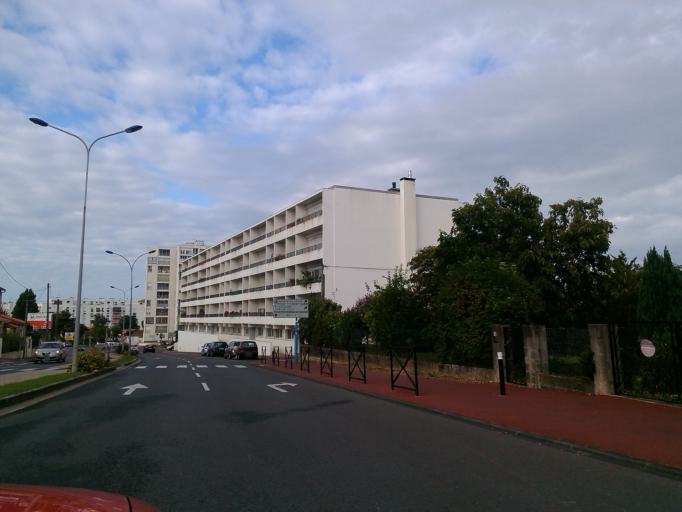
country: FR
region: Poitou-Charentes
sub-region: Departement de la Charente-Maritime
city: Royan
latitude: 45.6328
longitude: -1.0307
